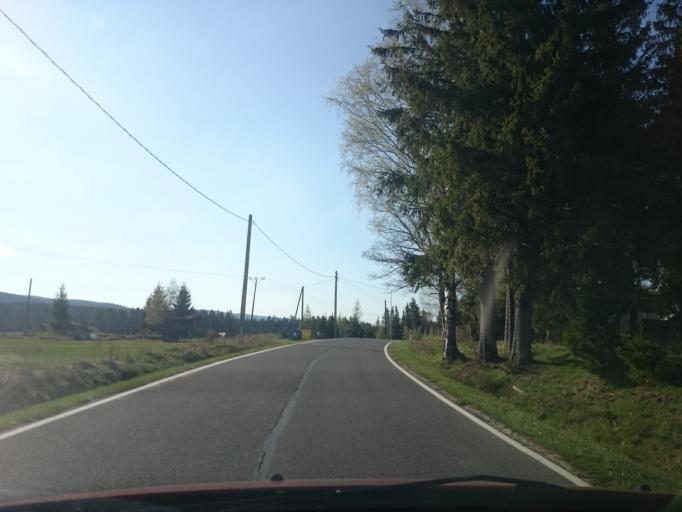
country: PL
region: Lower Silesian Voivodeship
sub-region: Powiat klodzki
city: Szczytna
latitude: 50.3173
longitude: 16.4417
